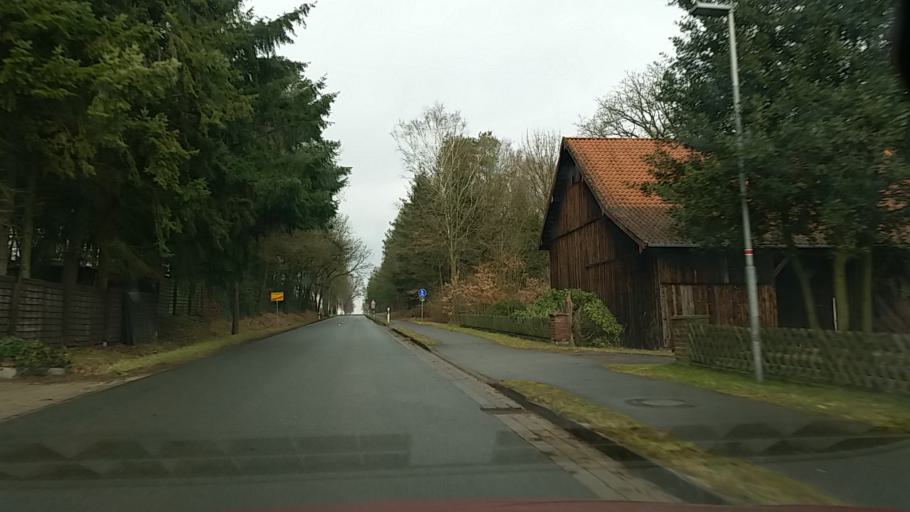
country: DE
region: Lower Saxony
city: Bispingen
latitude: 53.1062
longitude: 10.0027
